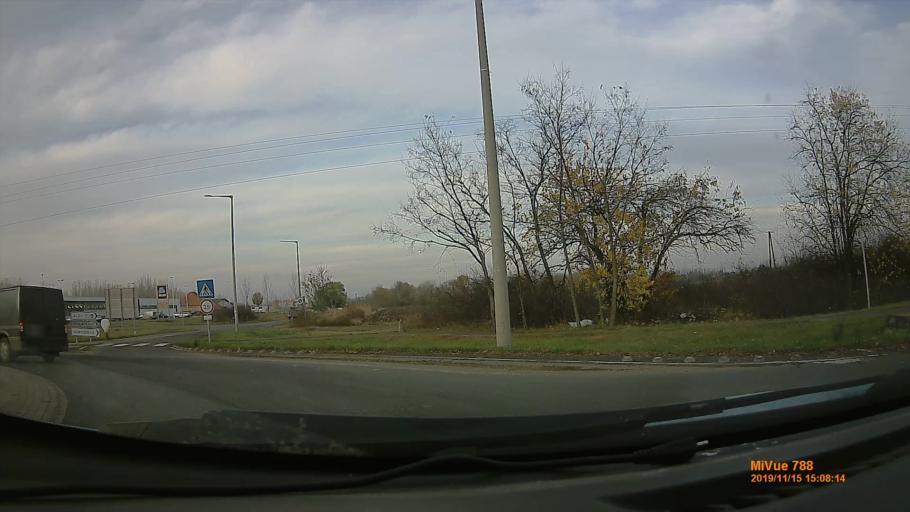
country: HU
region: Bekes
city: Gyula
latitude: 46.6529
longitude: 21.2386
